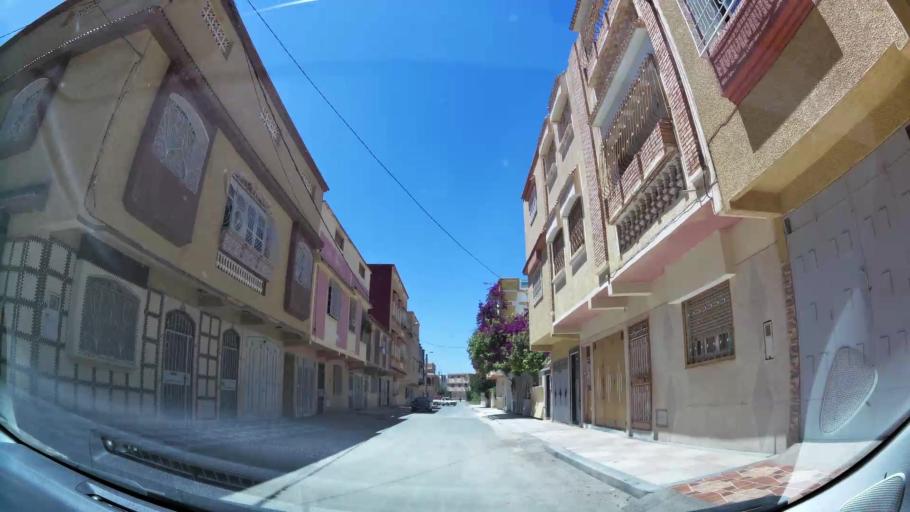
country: MA
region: Oriental
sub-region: Oujda-Angad
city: Oujda
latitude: 34.6781
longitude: -1.8745
